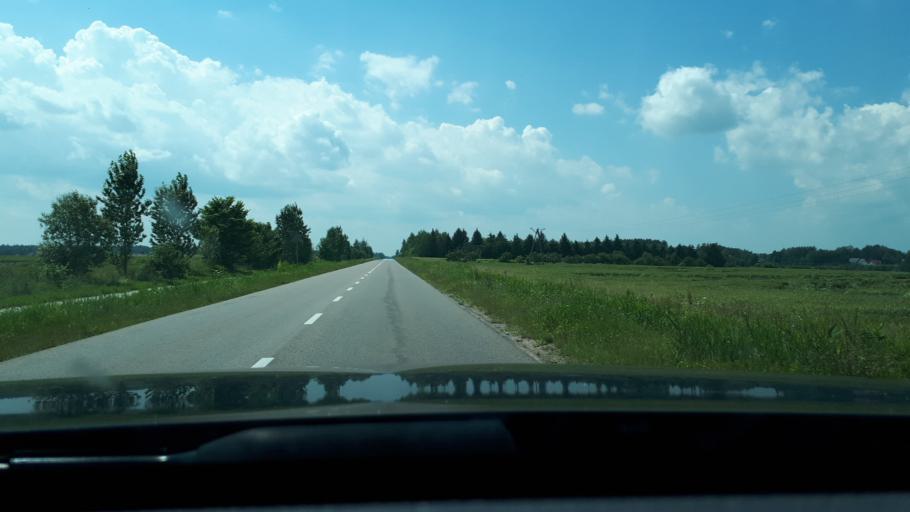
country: PL
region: Podlasie
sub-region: Powiat bialostocki
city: Choroszcz
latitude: 53.1292
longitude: 23.0151
